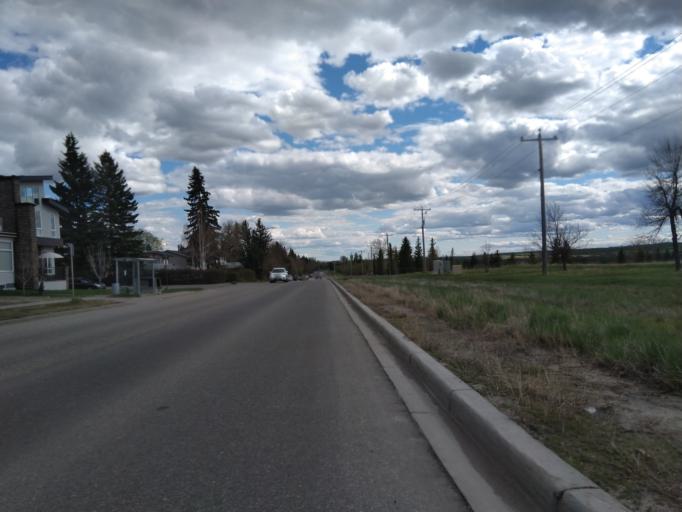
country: CA
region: Alberta
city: Calgary
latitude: 51.0014
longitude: -114.1411
